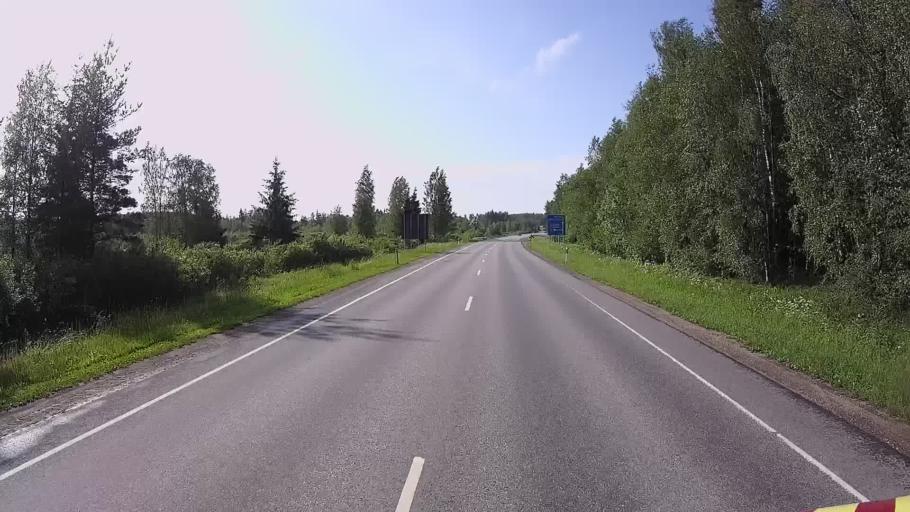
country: EE
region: Viljandimaa
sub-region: Viljandi linn
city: Viljandi
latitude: 58.3334
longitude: 25.5737
